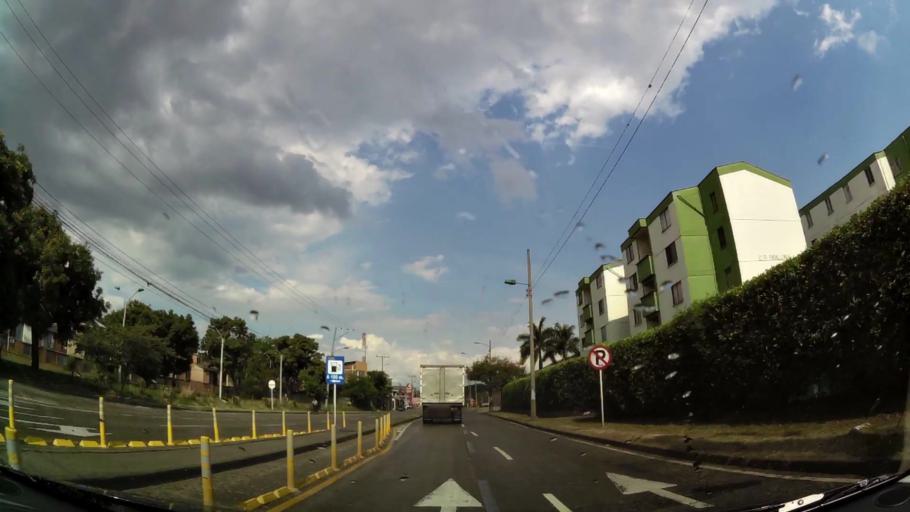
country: CO
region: Valle del Cauca
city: Cali
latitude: 3.4639
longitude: -76.4967
